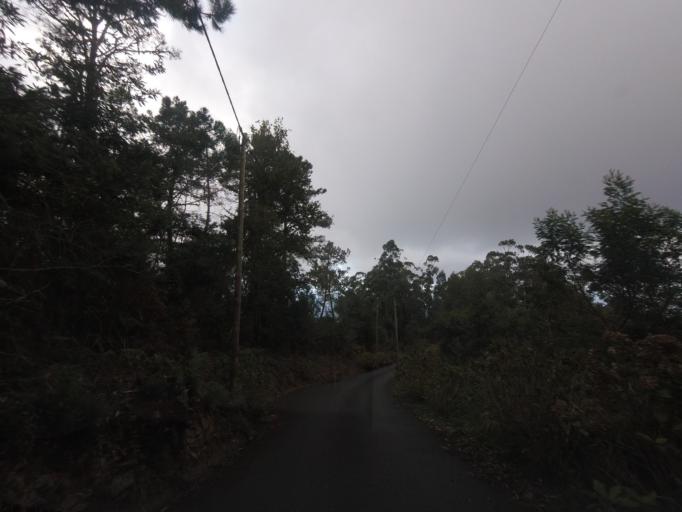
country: PT
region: Madeira
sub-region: Santana
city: Santana
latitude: 32.7910
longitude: -16.8948
